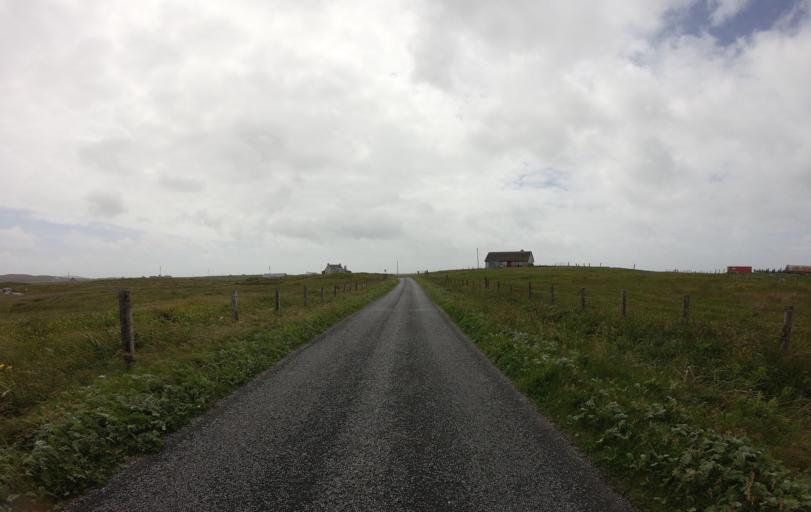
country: GB
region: Scotland
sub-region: Eilean Siar
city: Isle of South Uist
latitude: 57.2542
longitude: -7.4053
